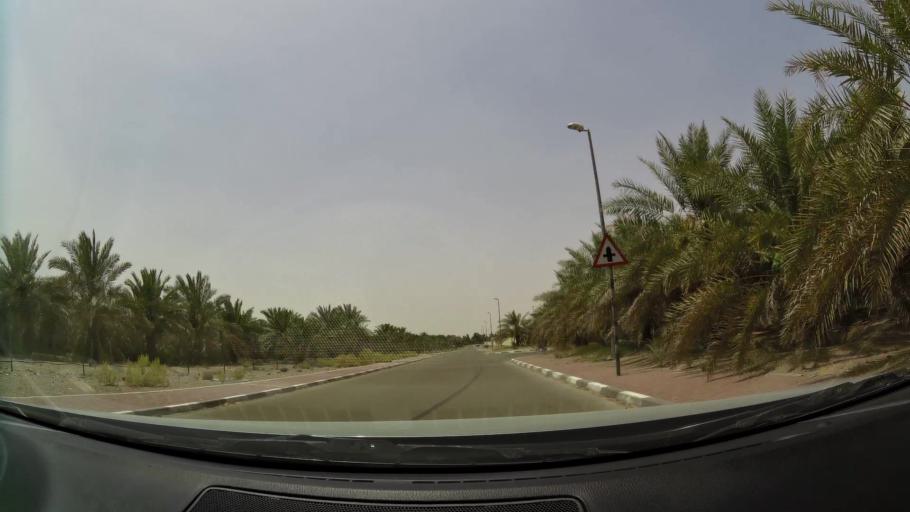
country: AE
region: Abu Dhabi
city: Al Ain
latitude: 24.1996
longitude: 55.7052
